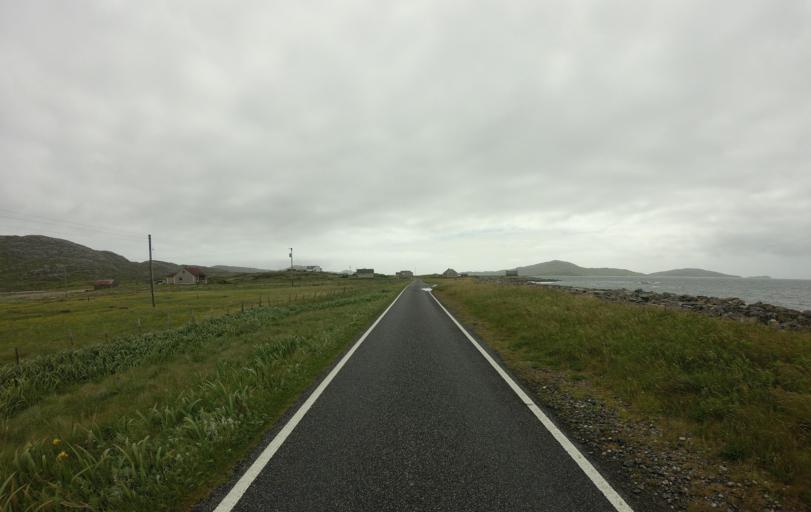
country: GB
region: Scotland
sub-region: Eilean Siar
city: Isle of South Uist
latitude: 57.1037
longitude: -7.3453
